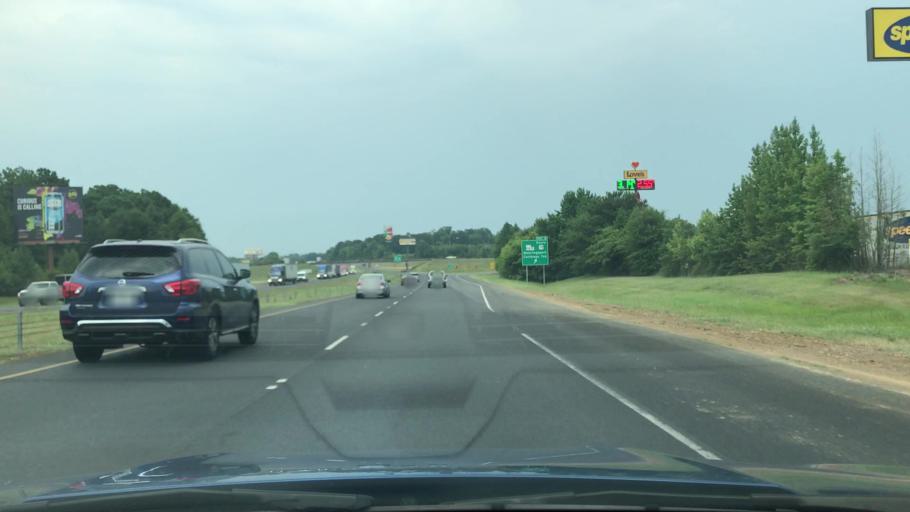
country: US
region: Louisiana
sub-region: Caddo Parish
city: Greenwood
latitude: 32.4482
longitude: -93.9857
